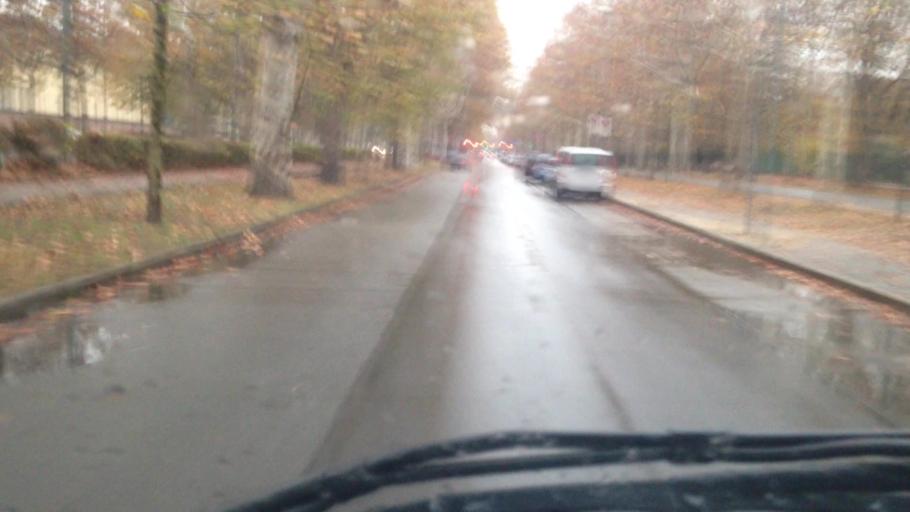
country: IT
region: Piedmont
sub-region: Provincia di Torino
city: Lesna
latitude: 45.0468
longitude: 7.6518
